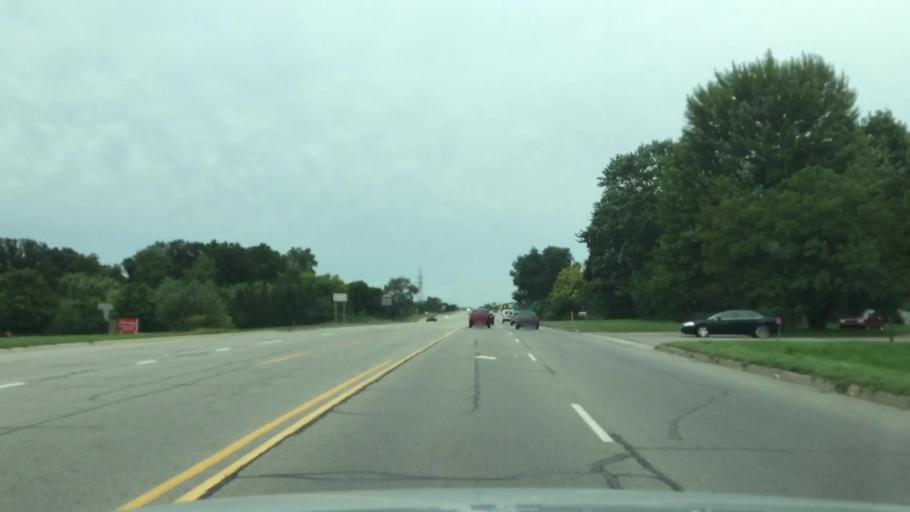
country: US
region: Michigan
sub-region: Washtenaw County
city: Ypsilanti
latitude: 42.2280
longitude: -83.6441
